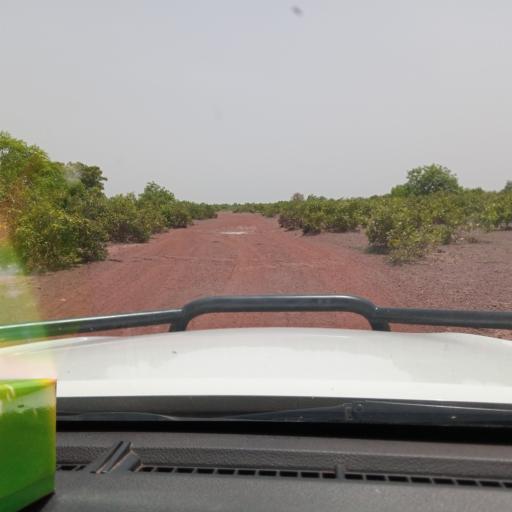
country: ML
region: Koulikoro
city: Koulikoro
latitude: 13.1095
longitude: -7.6158
